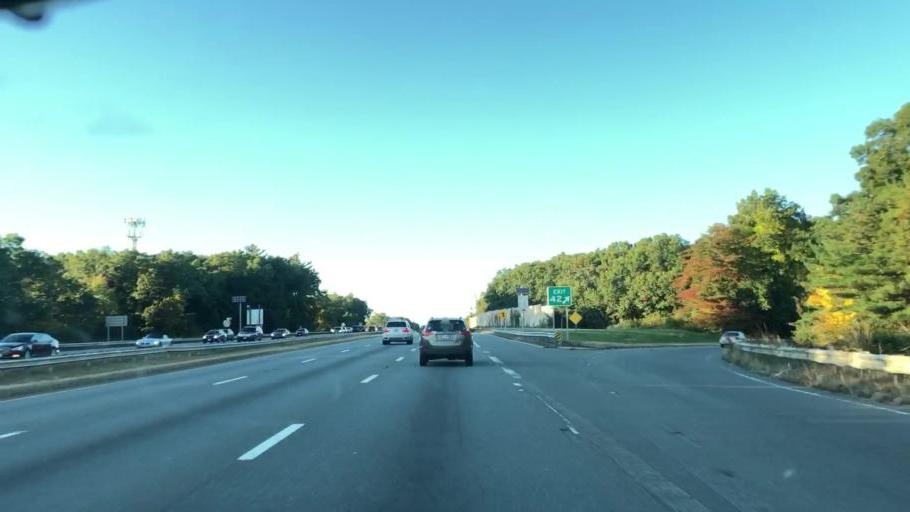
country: US
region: Massachusetts
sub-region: Essex County
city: Andover
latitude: 42.6222
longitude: -71.1769
